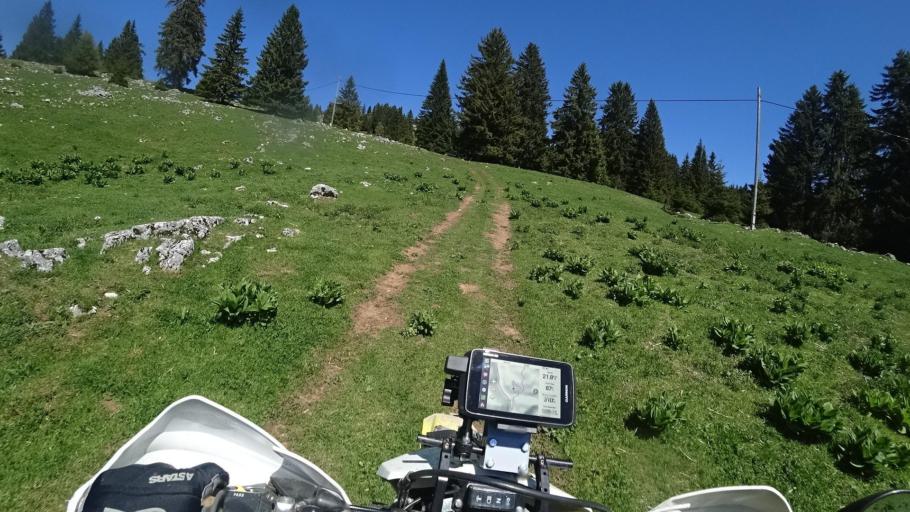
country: BA
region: Federation of Bosnia and Herzegovina
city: Turbe
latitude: 44.2820
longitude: 17.6071
